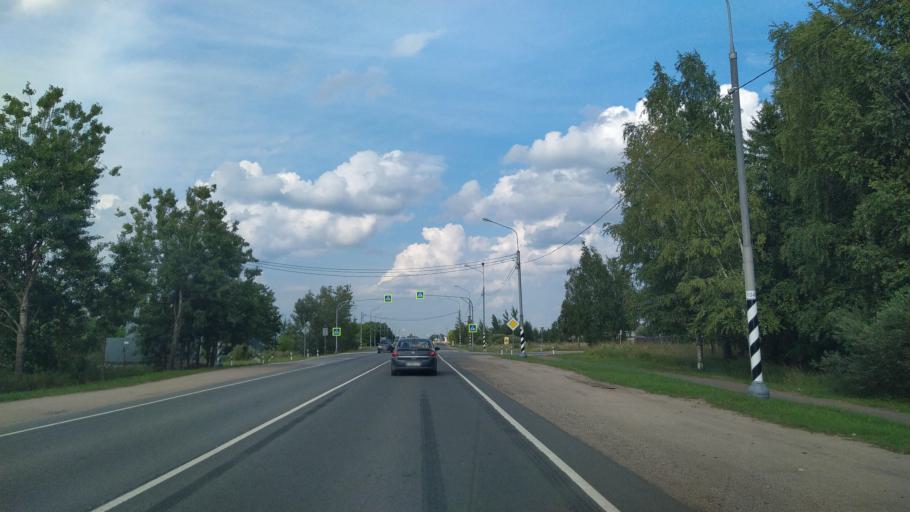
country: RU
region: Novgorod
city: Shimsk
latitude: 58.2156
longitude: 30.7308
